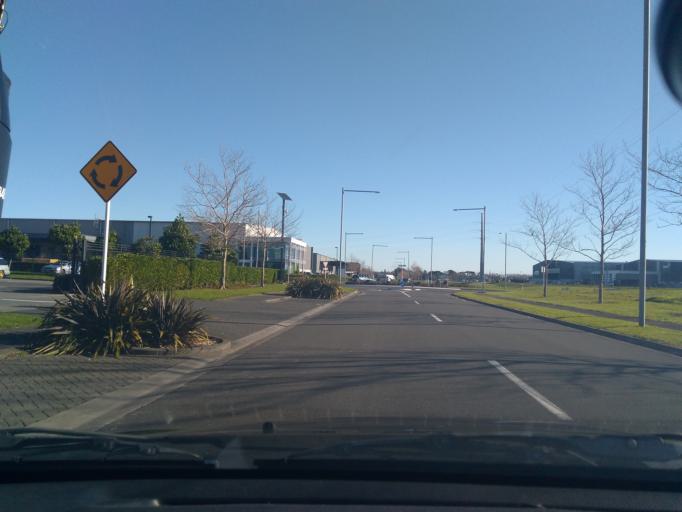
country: NZ
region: Auckland
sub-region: Auckland
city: Tamaki
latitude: -36.9295
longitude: 174.8749
